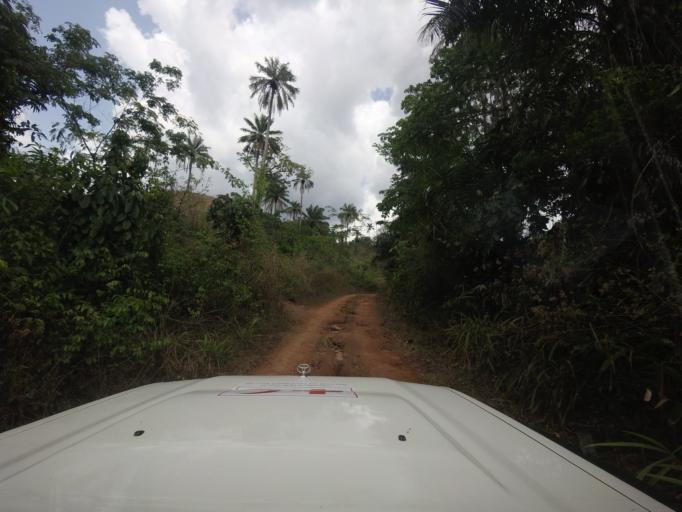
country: LR
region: Lofa
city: Voinjama
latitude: 8.3952
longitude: -9.6308
